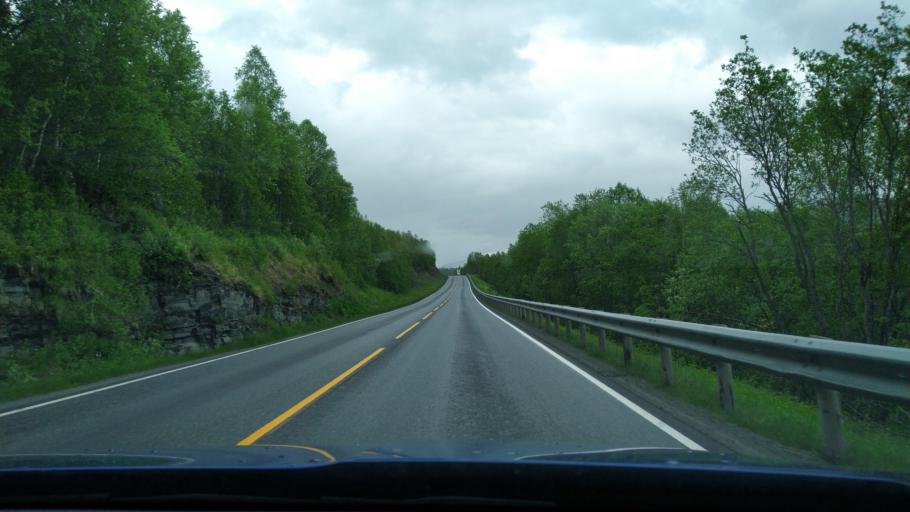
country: NO
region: Troms
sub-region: Malselv
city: Moen
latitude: 69.1162
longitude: 18.9180
